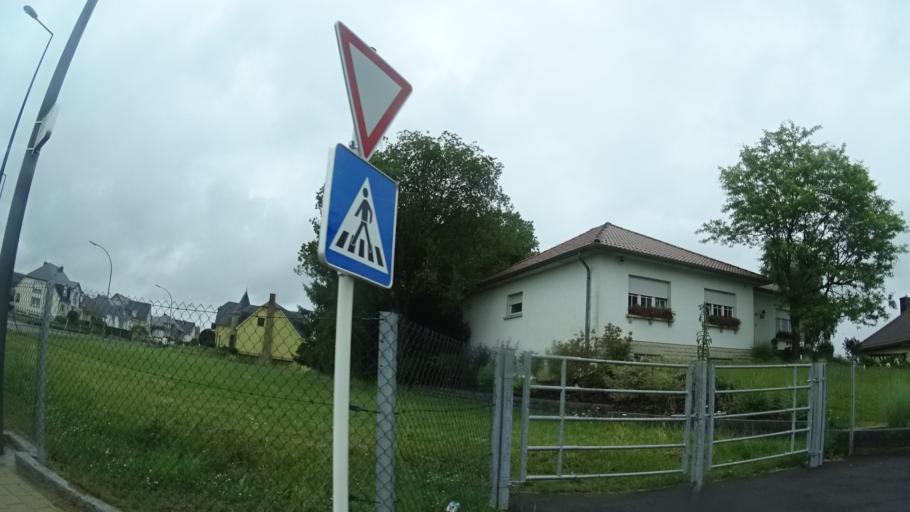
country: LU
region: Luxembourg
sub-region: Canton de Capellen
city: Bascharage
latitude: 49.5715
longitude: 5.9009
